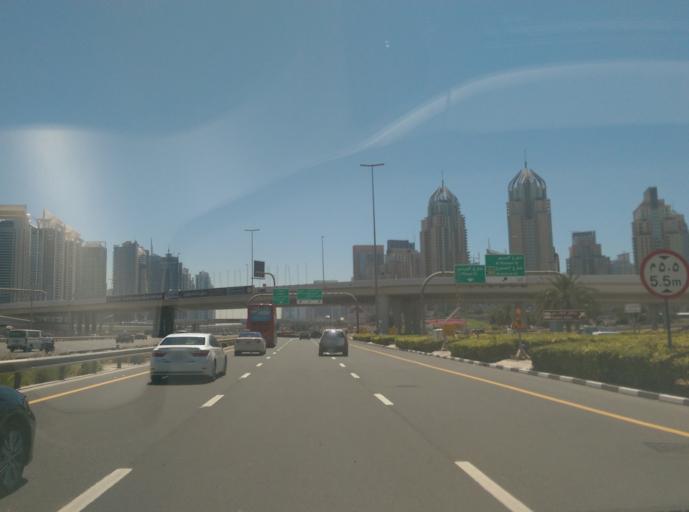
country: AE
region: Dubai
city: Dubai
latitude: 25.0879
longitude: 55.1555
